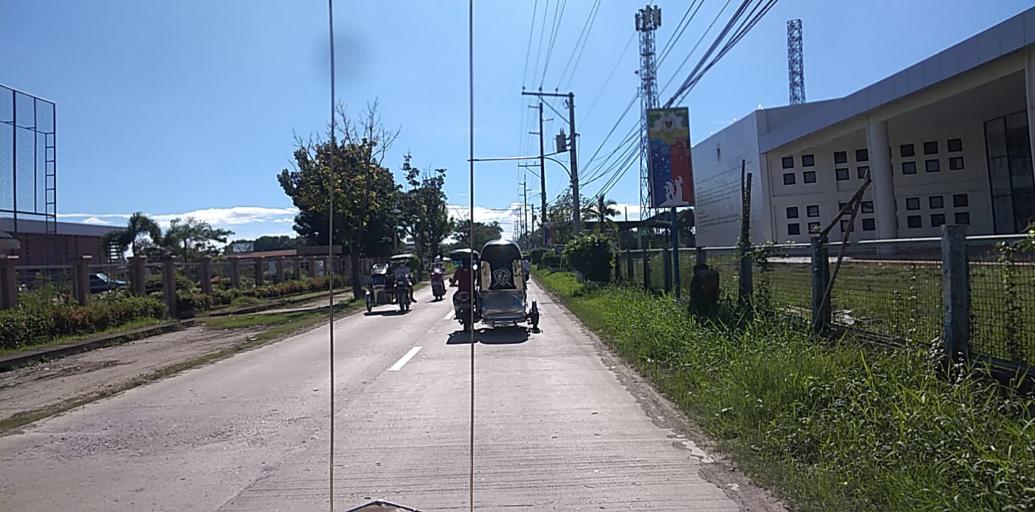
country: PH
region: Central Luzon
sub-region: Province of Pampanga
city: San Luis
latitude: 15.0481
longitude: 120.7847
